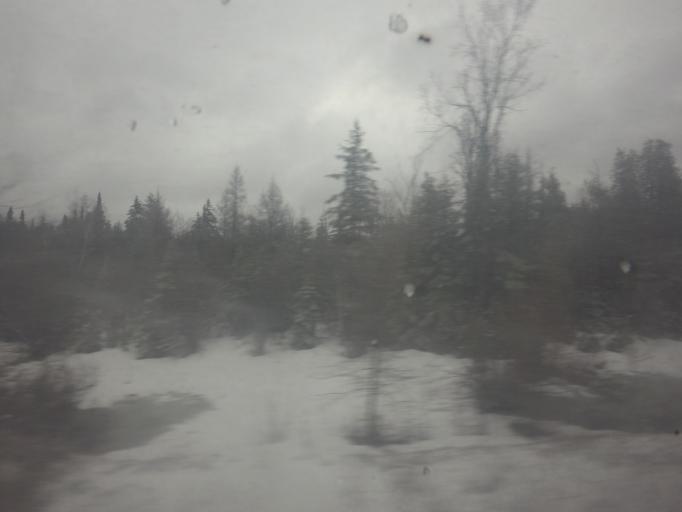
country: CA
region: Ontario
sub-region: Lanark County
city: Smiths Falls
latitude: 45.0023
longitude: -75.9614
